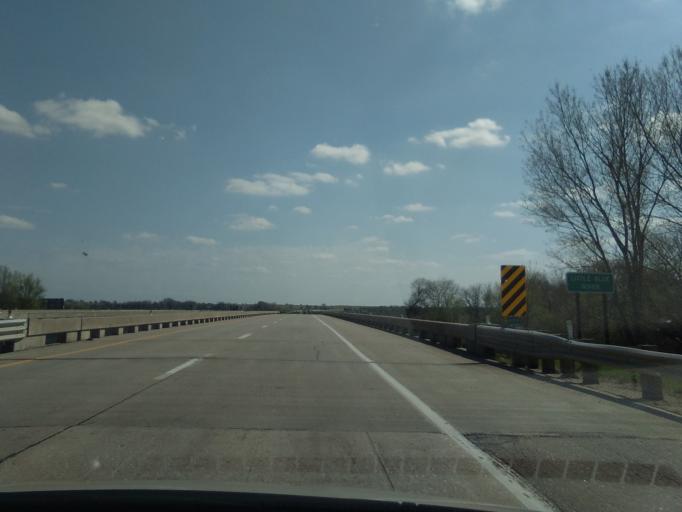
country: US
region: Nebraska
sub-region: Thayer County
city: Hebron
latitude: 40.1598
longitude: -97.5709
